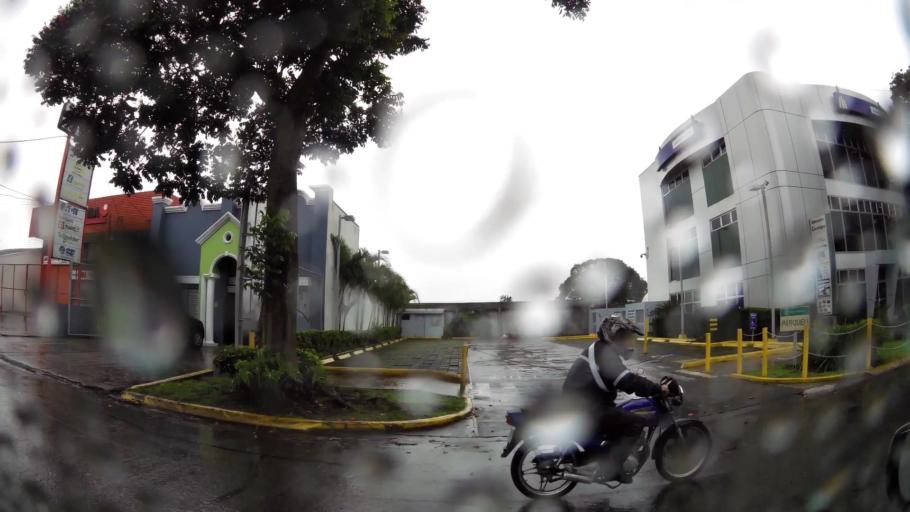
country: CR
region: Cartago
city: Cartago
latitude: 9.8668
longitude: -83.9302
